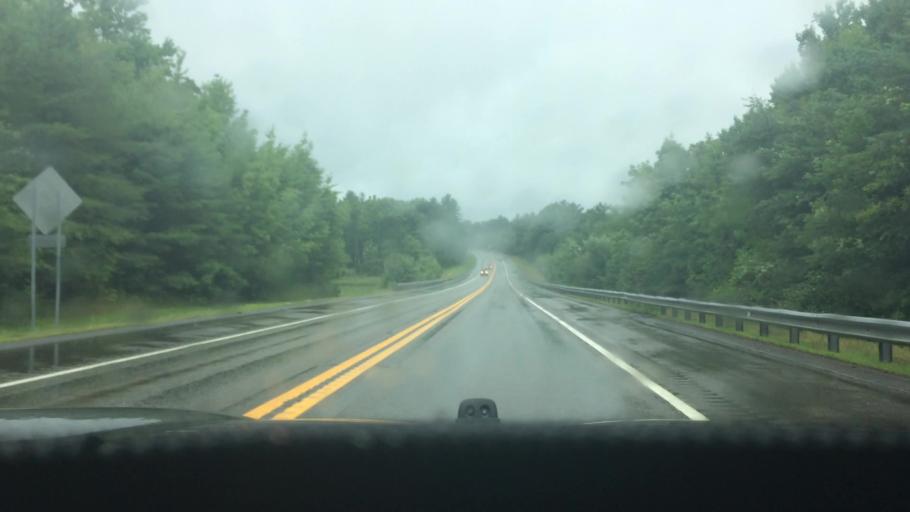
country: US
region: Massachusetts
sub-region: Worcester County
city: South Ashburnham
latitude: 42.5792
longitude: -71.9518
